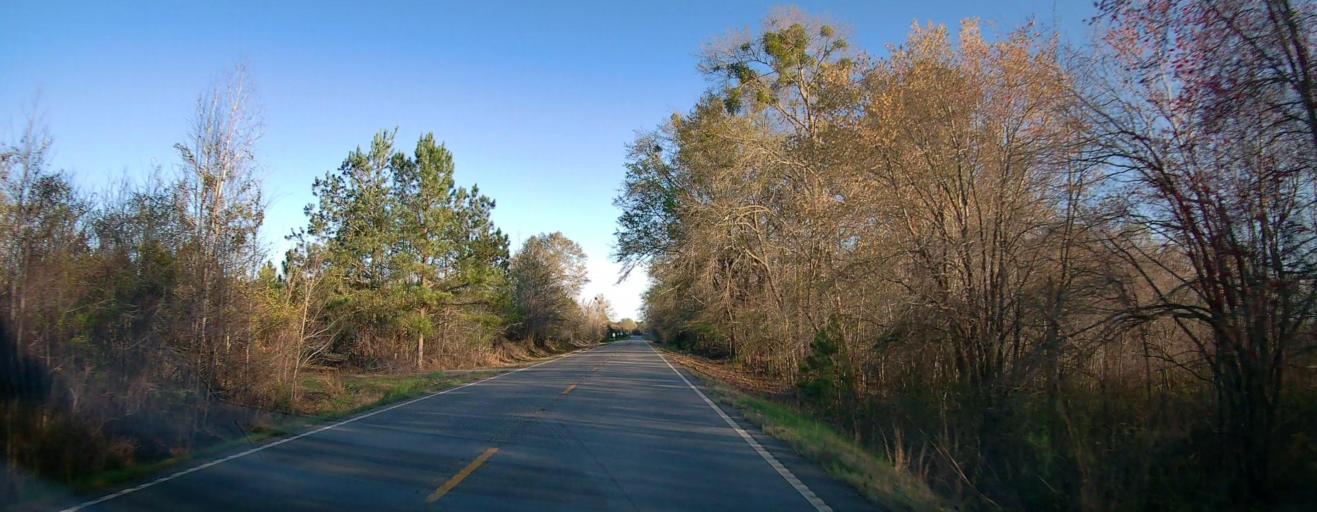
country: US
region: Georgia
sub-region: Wilcox County
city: Abbeville
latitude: 32.1195
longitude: -83.3267
